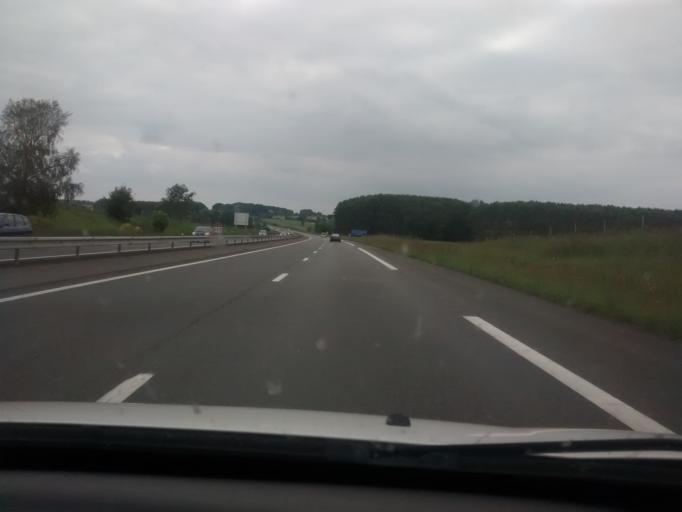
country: FR
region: Pays de la Loire
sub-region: Departement de la Sarthe
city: Trange
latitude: 48.0453
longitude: 0.1133
